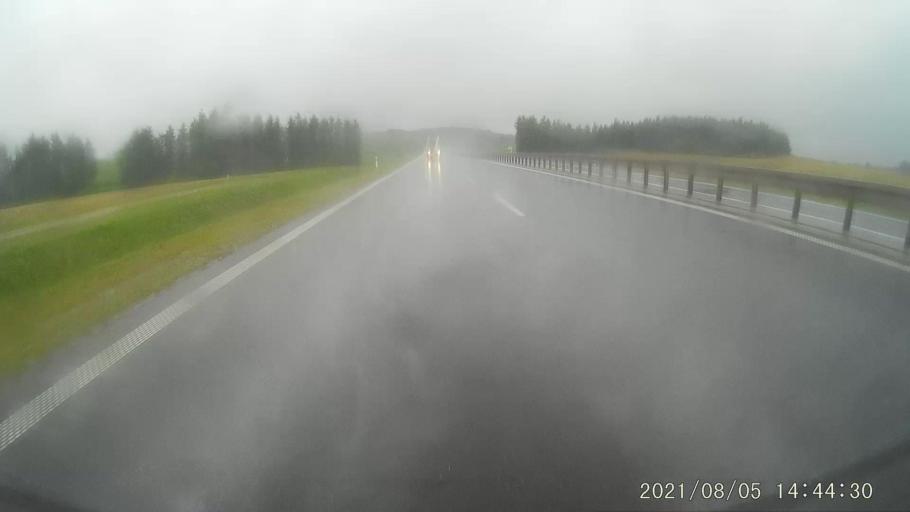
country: PL
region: Opole Voivodeship
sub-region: Powiat nyski
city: Nysa
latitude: 50.4945
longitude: 17.3770
